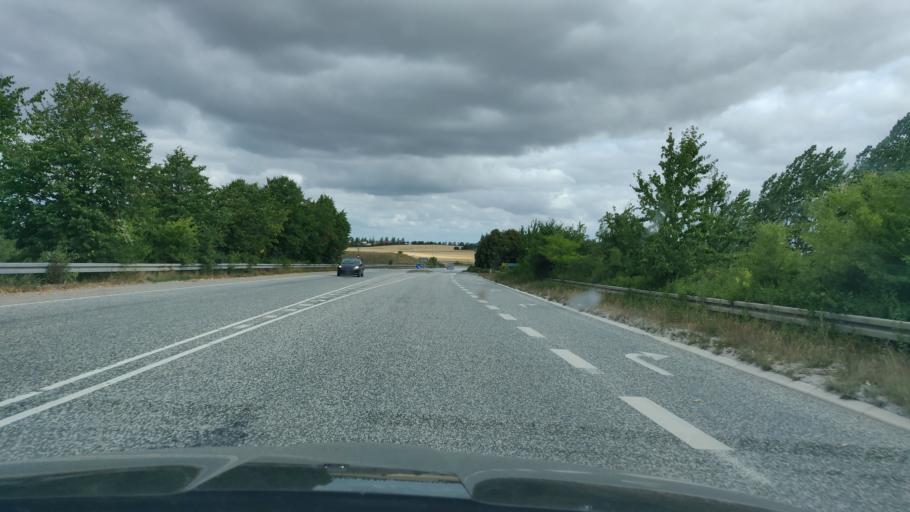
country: DK
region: Capital Region
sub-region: Hoje-Taastrup Kommune
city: Flong
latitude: 55.6505
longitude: 12.1586
